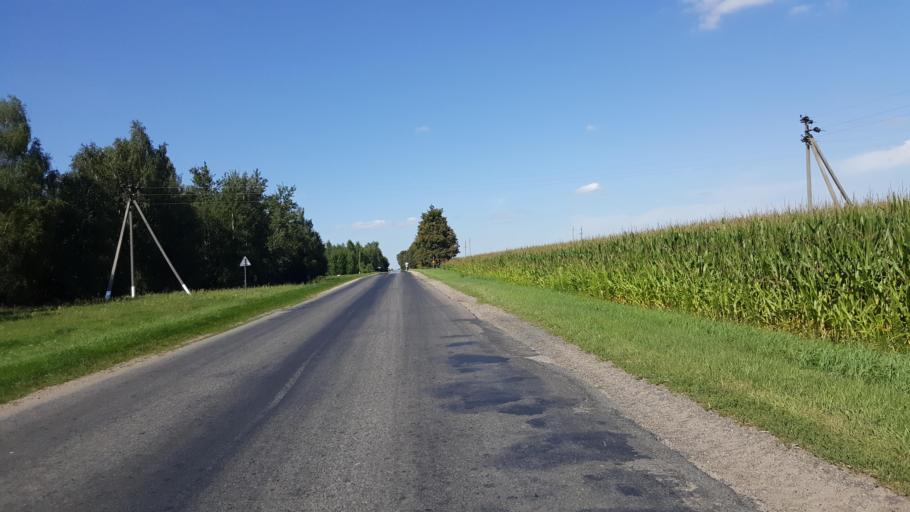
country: BY
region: Brest
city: Charnawchytsy
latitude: 52.2810
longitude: 23.6030
